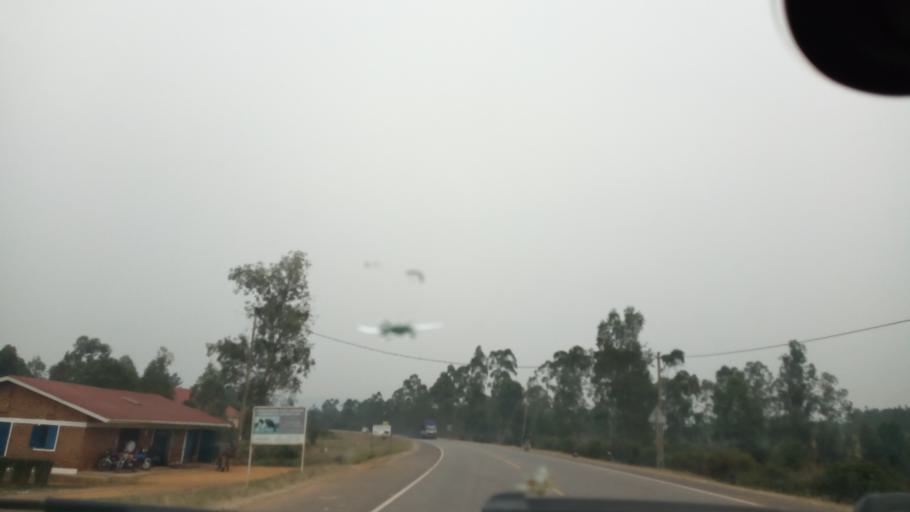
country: UG
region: Western Region
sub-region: Mbarara District
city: Mbarara
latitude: -0.7288
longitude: 30.7335
